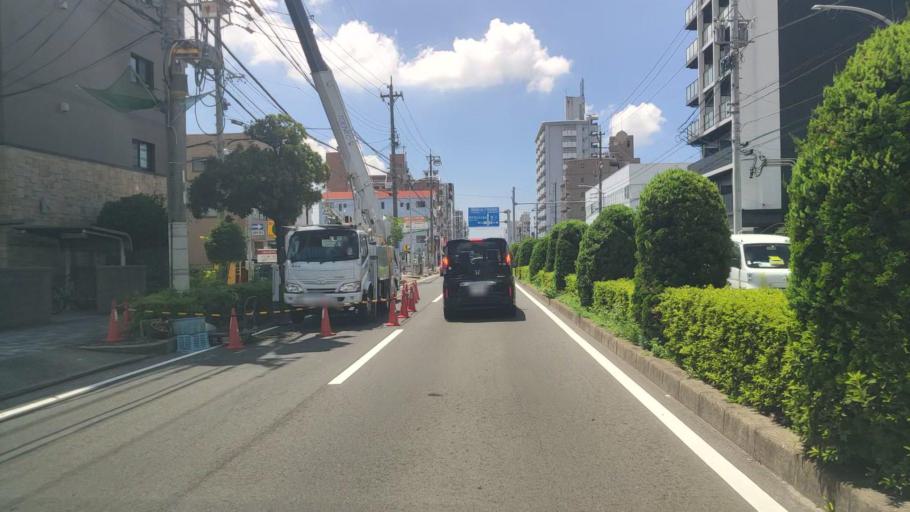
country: JP
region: Aichi
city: Kanie
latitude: 35.1426
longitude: 136.8534
